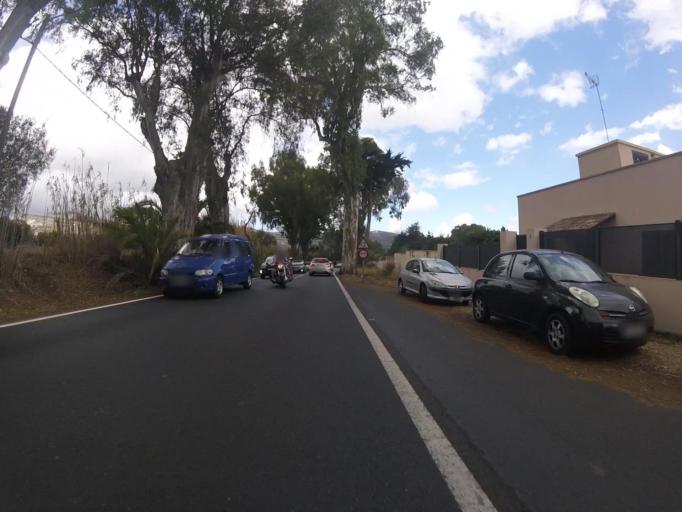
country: ES
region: Canary Islands
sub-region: Provincia de Las Palmas
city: Santa Brigida
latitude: 28.0274
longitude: -15.5093
